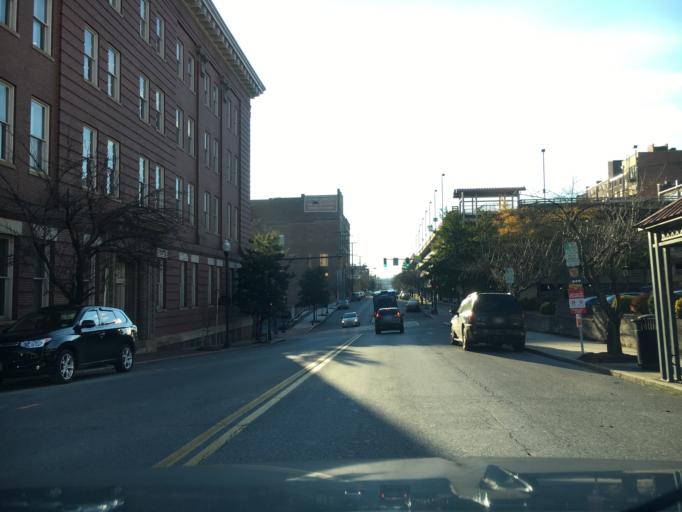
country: US
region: Virginia
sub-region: City of Lynchburg
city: Lynchburg
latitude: 37.4158
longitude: -79.1418
